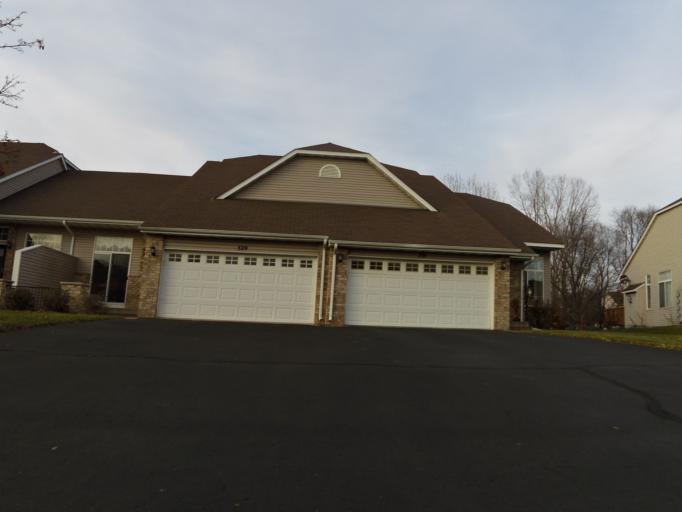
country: US
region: Wisconsin
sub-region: Saint Croix County
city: Hudson
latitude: 44.9757
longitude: -92.7351
